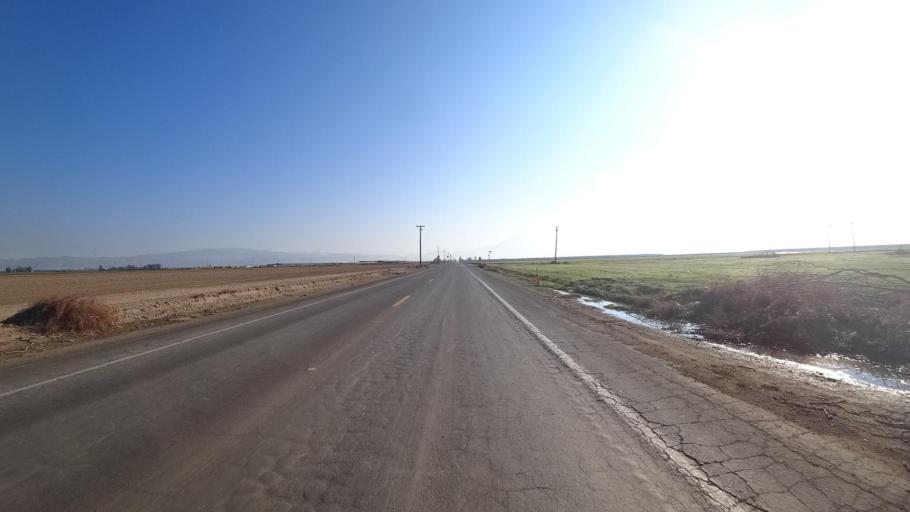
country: US
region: California
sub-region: Kern County
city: Lamont
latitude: 35.2524
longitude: -118.9556
